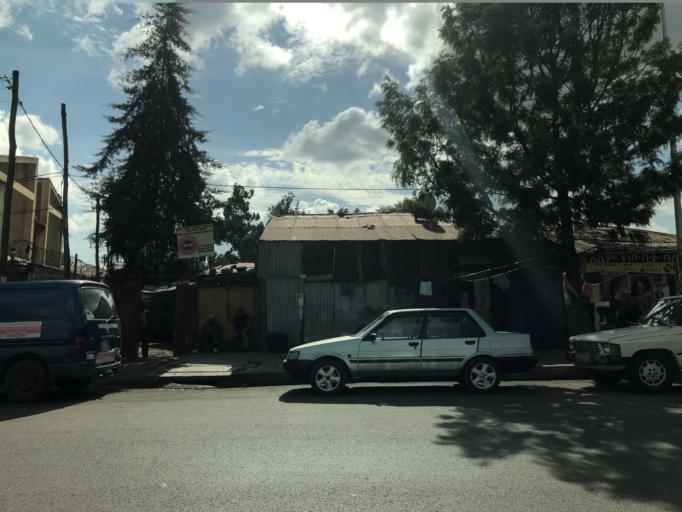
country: ET
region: Adis Abeba
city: Addis Ababa
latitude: 9.0259
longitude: 38.7763
